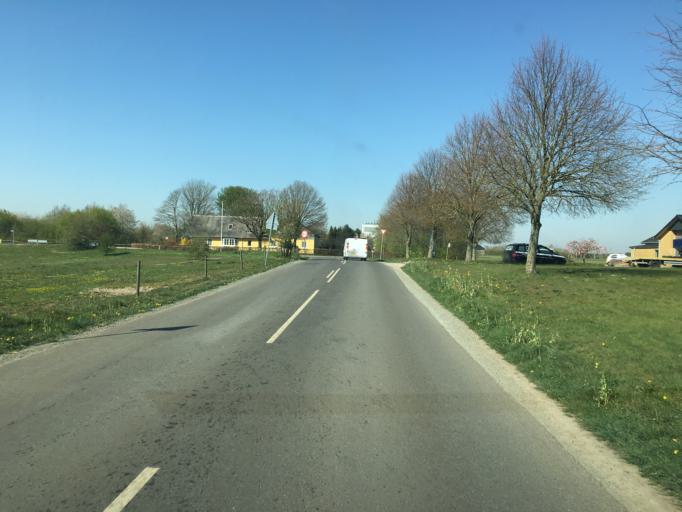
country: DK
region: South Denmark
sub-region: Aabenraa Kommune
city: Rodekro
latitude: 55.0695
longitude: 9.2991
